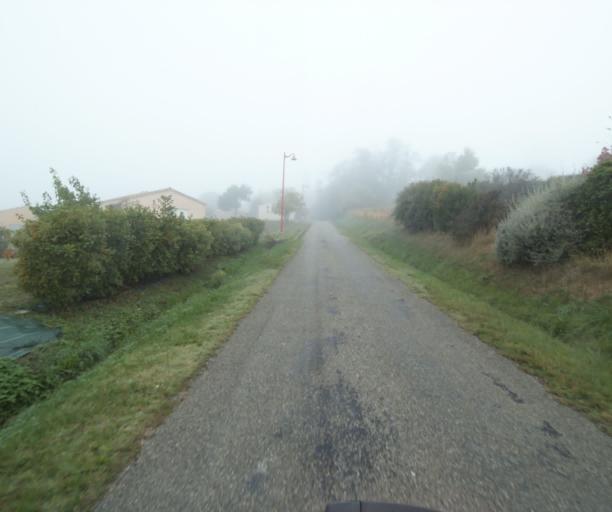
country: FR
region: Midi-Pyrenees
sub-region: Departement du Tarn-et-Garonne
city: Nohic
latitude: 43.9205
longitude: 1.4735
